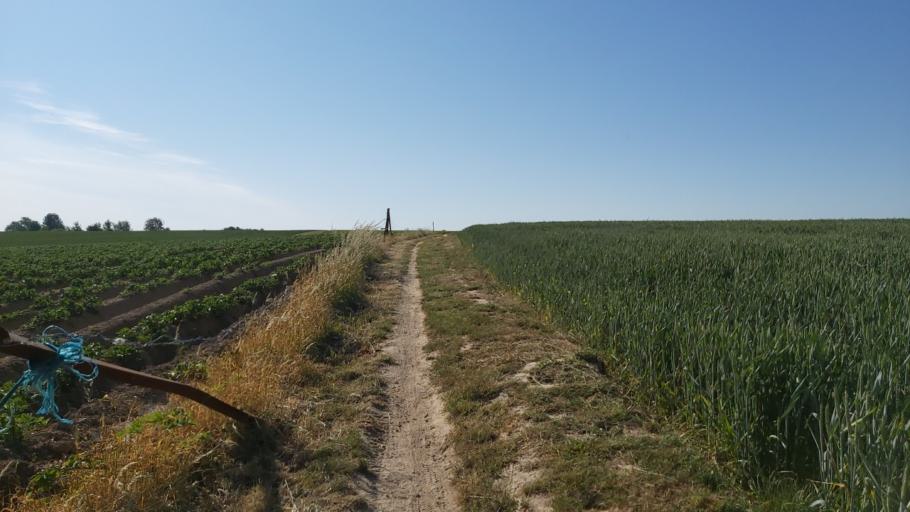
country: BE
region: Flanders
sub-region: Provincie Vlaams-Brabant
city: Hoegaarden
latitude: 50.7655
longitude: 4.8572
